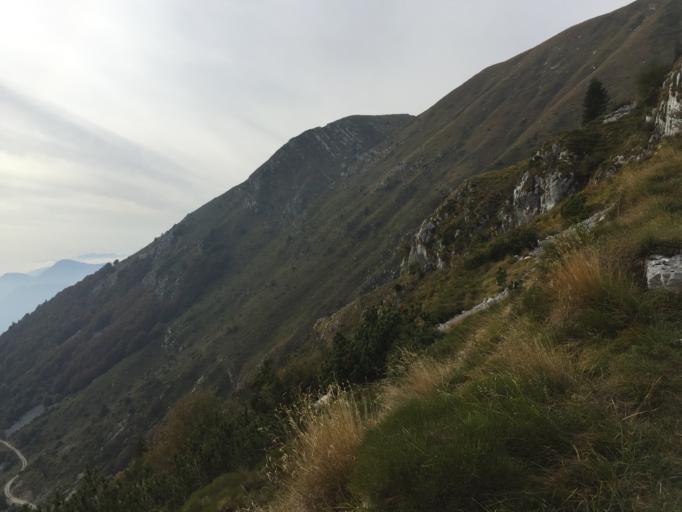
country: IT
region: Friuli Venezia Giulia
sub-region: Provincia di Udine
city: Resiutta
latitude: 46.3460
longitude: 13.2129
